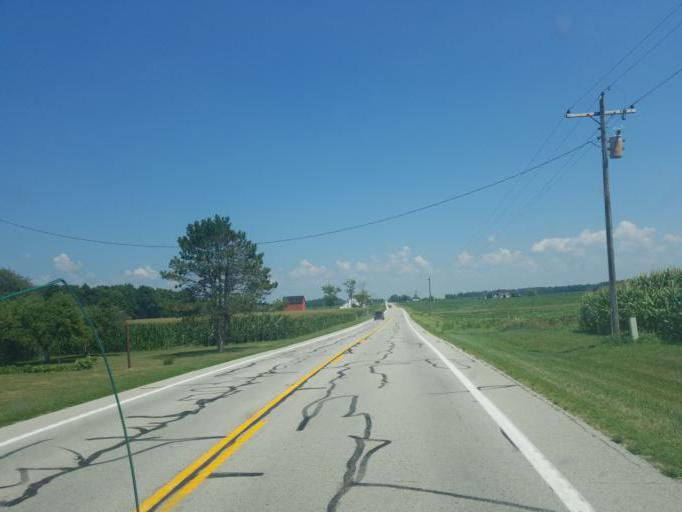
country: US
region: Ohio
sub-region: Shelby County
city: Anna
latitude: 40.3953
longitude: -84.1292
